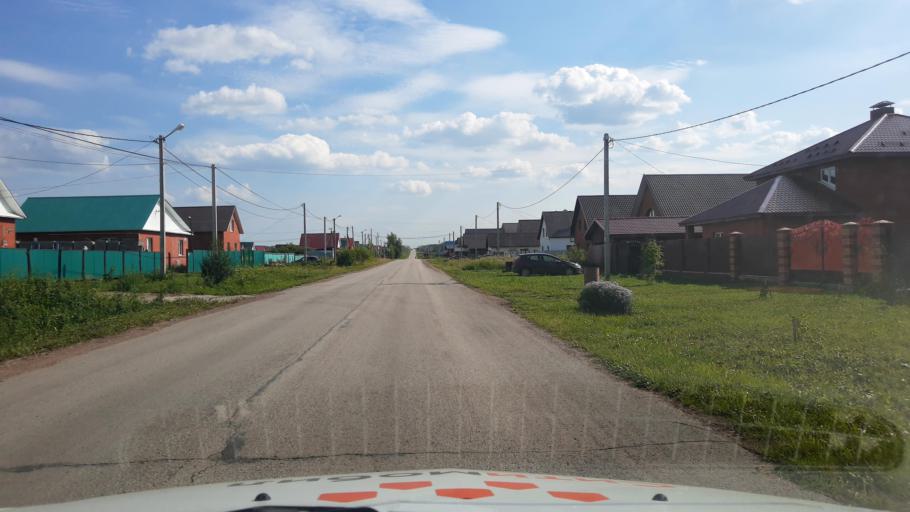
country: RU
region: Bashkortostan
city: Kabakovo
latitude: 54.6629
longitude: 56.2139
